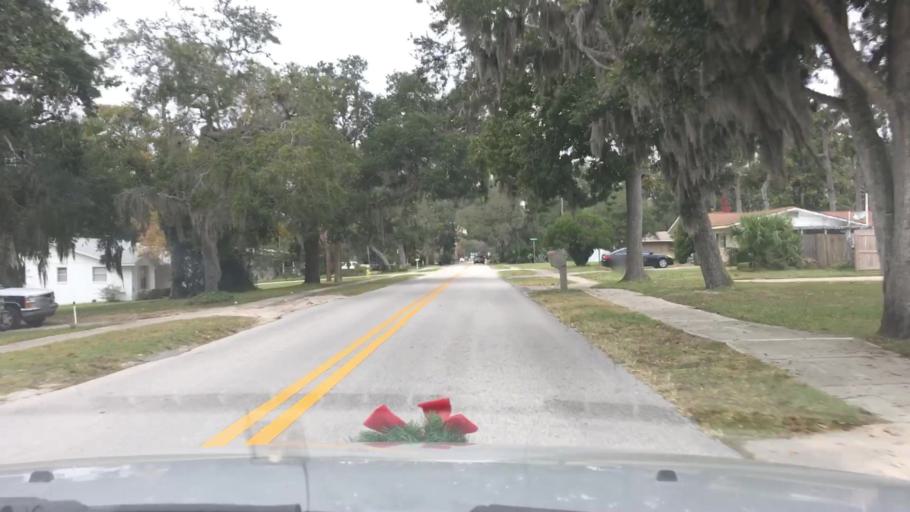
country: US
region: Florida
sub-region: Volusia County
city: Ormond Beach
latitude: 29.2963
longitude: -81.0644
